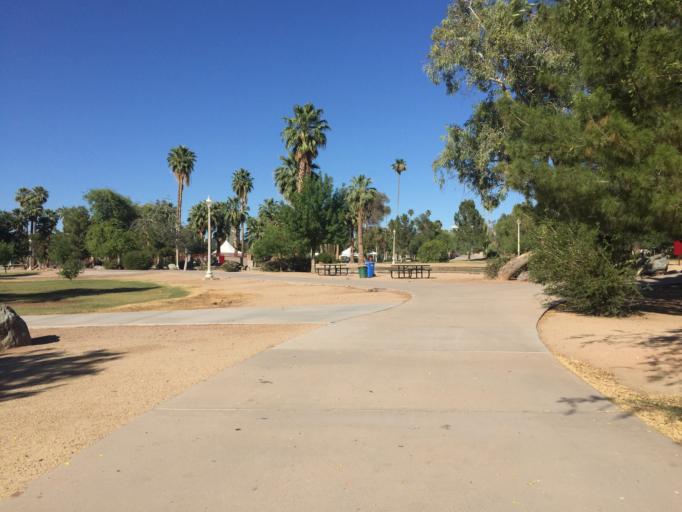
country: US
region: Arizona
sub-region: Maricopa County
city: Phoenix
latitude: 33.4746
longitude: -112.0900
